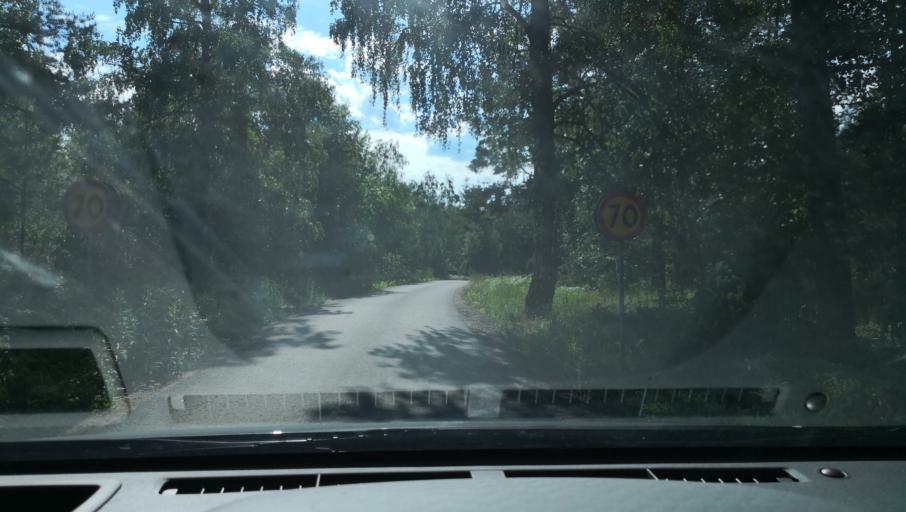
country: SE
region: Uppsala
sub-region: Enkopings Kommun
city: Orsundsbro
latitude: 59.8391
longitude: 17.2724
